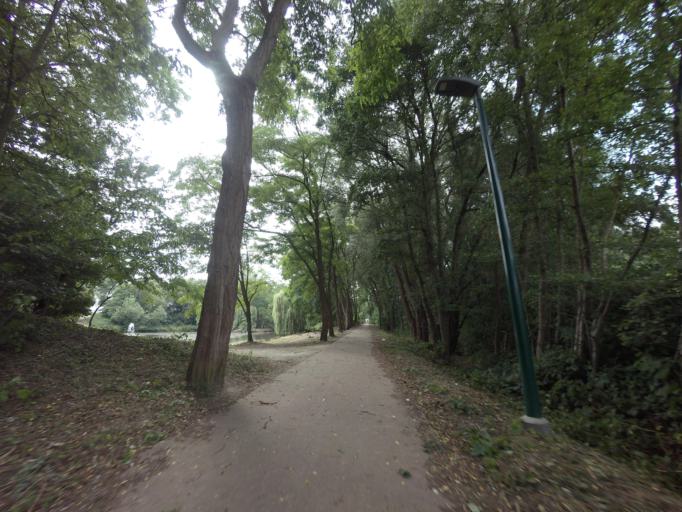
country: BE
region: Flanders
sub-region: Provincie Vlaams-Brabant
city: Grimbergen
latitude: 50.9137
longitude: 4.3634
